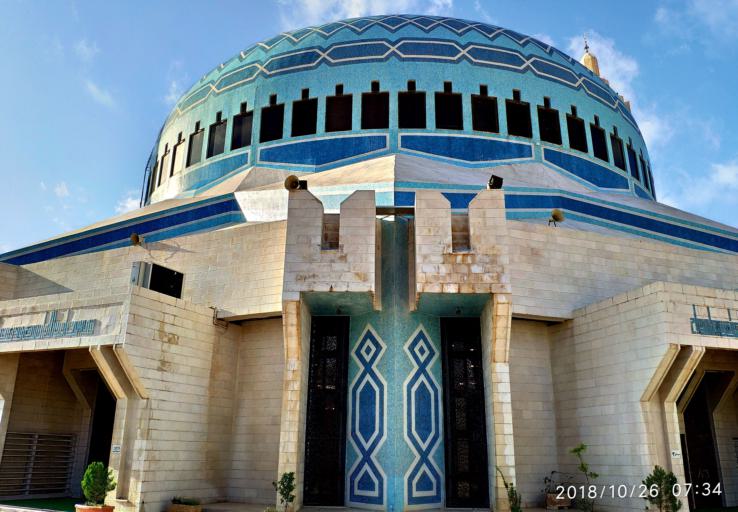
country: JO
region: Amman
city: Amman
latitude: 31.9613
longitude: 35.9129
